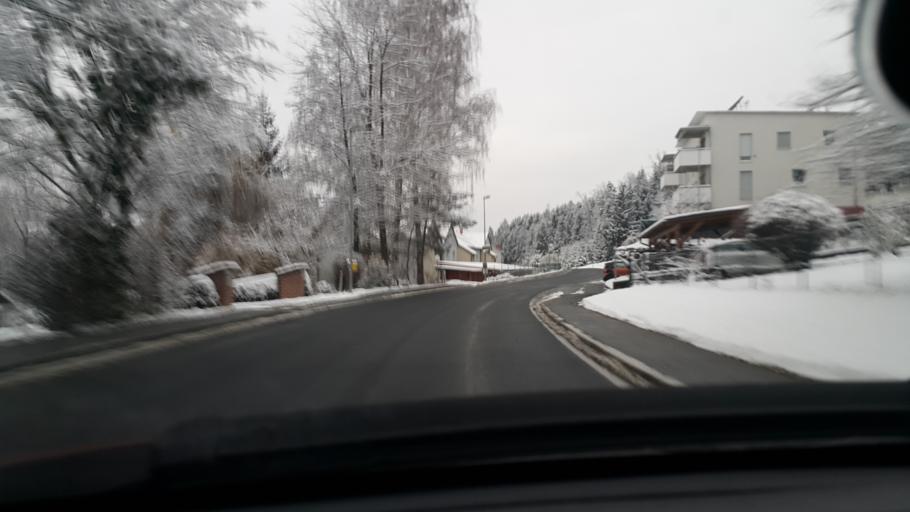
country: AT
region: Styria
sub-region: Politischer Bezirk Graz-Umgebung
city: Hitzendorf
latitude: 47.0556
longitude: 15.2854
